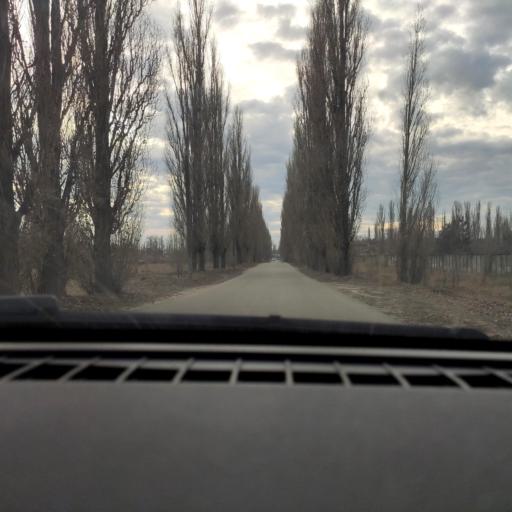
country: RU
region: Voronezj
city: Maslovka
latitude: 51.6020
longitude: 39.2207
